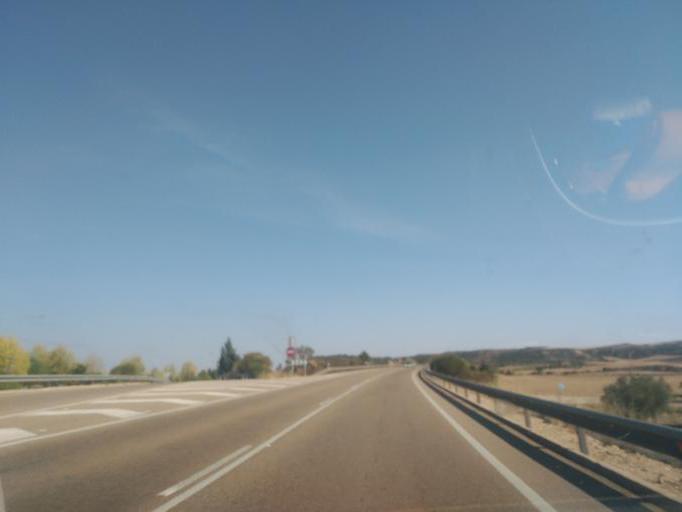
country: ES
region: Castille and Leon
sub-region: Provincia de Valladolid
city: Quintanilla de Arriba
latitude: 41.6199
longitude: -4.2293
